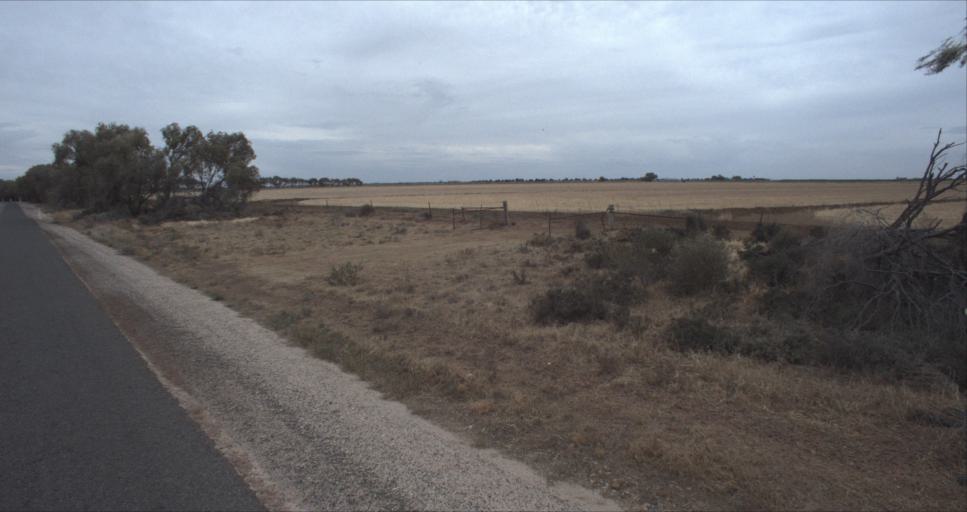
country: AU
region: New South Wales
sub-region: Leeton
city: Leeton
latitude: -34.4736
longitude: 146.3962
